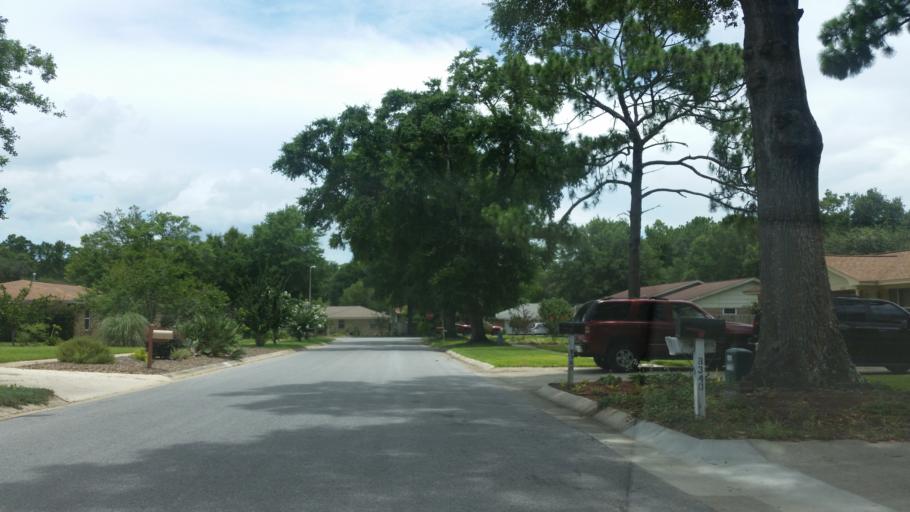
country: US
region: Florida
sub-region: Escambia County
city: Ferry Pass
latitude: 30.5141
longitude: -87.1854
